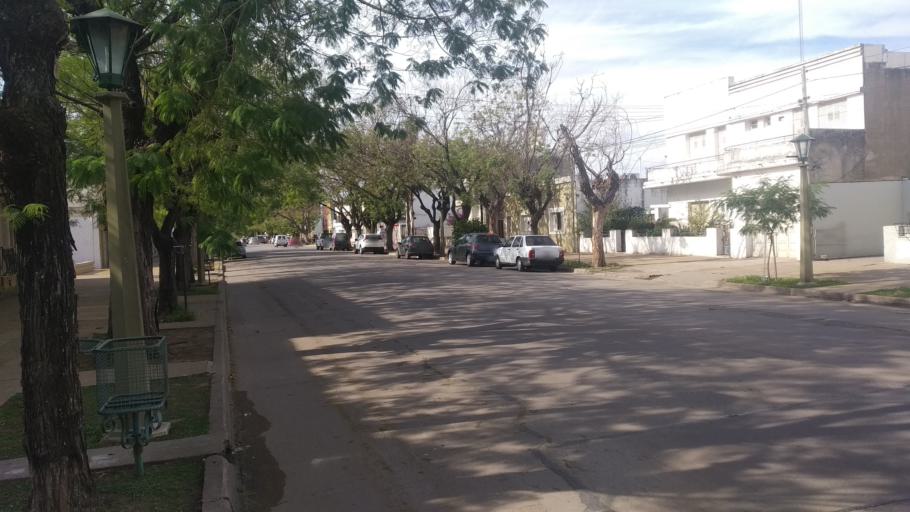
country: AR
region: Cordoba
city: Leones
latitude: -32.6594
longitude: -62.3005
